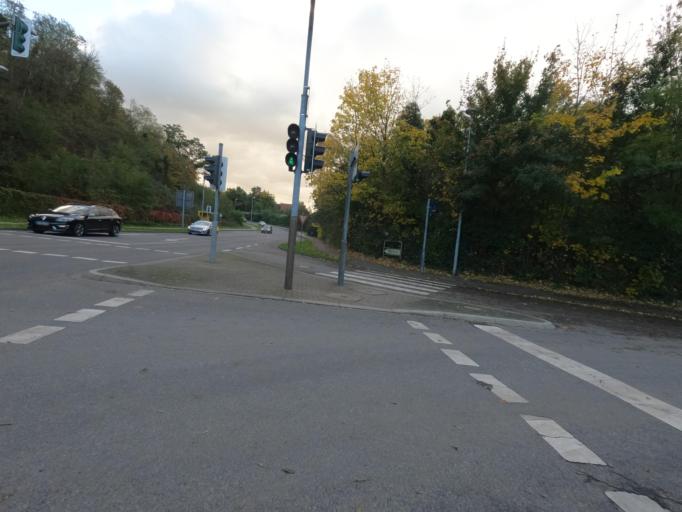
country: DE
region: North Rhine-Westphalia
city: Huckelhoven
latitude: 51.0614
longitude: 6.2106
